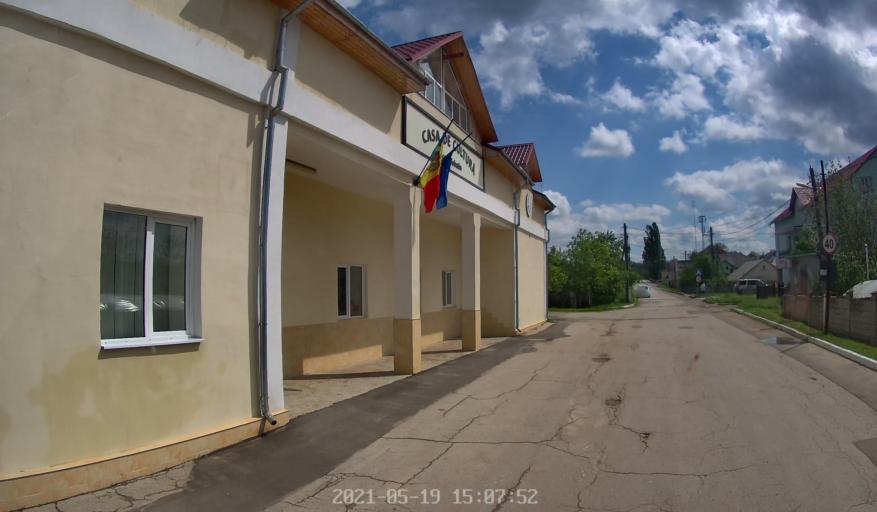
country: MD
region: Chisinau
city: Stauceni
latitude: 47.0626
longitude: 28.9485
